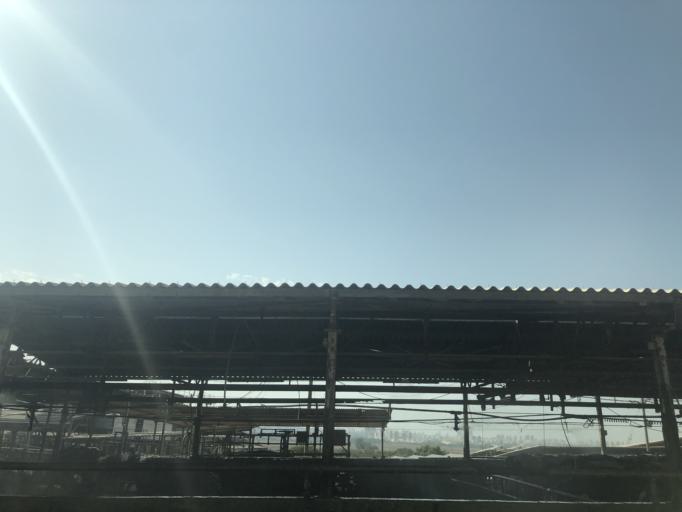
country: IL
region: Central District
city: Rosh Ha'Ayin
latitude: 32.0592
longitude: 34.9484
